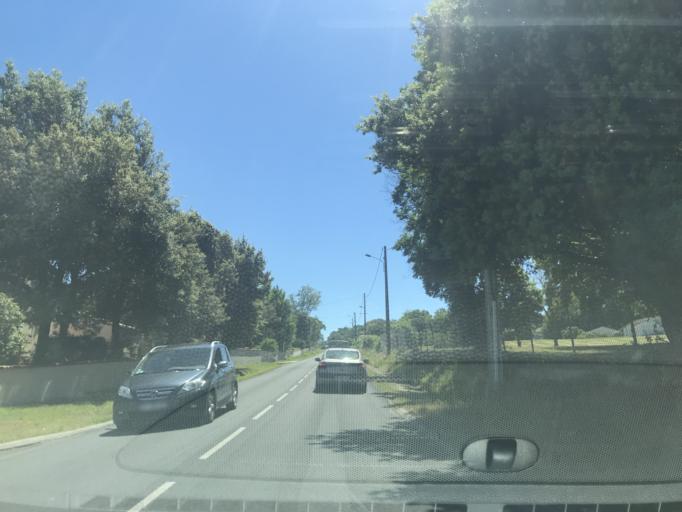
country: FR
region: Poitou-Charentes
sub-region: Departement de la Charente-Maritime
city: Meschers-sur-Gironde
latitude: 45.5696
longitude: -0.9606
